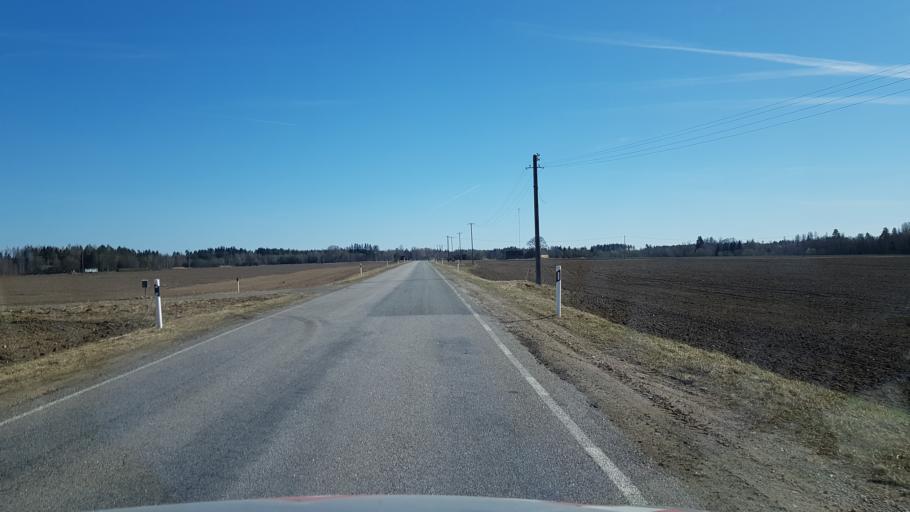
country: EE
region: Laeaene-Virumaa
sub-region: Vinni vald
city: Vinni
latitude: 59.2409
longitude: 26.6921
